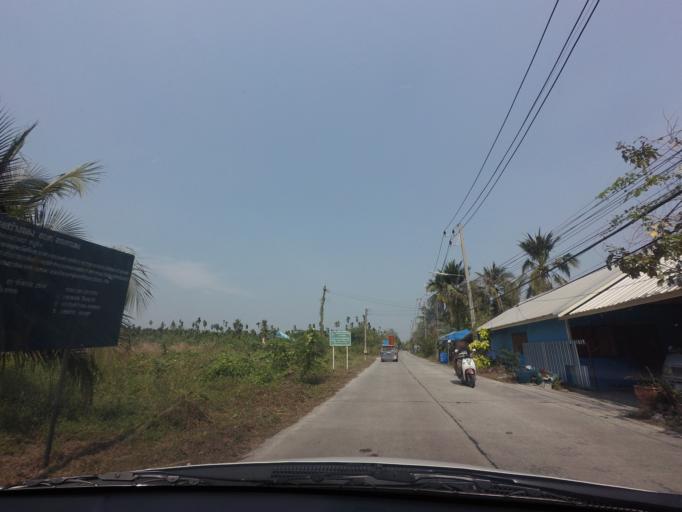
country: TH
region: Nakhon Pathom
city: Sam Phran
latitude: 13.7583
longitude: 100.2533
